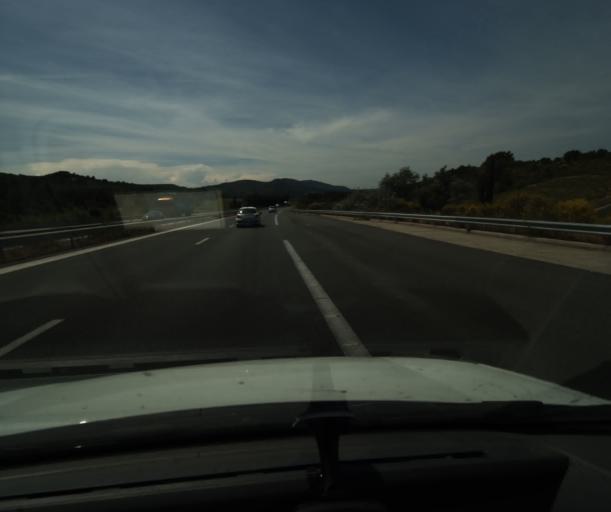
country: FR
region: Languedoc-Roussillon
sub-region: Departement de l'Aude
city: Puicheric
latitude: 43.1705
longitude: 2.6165
